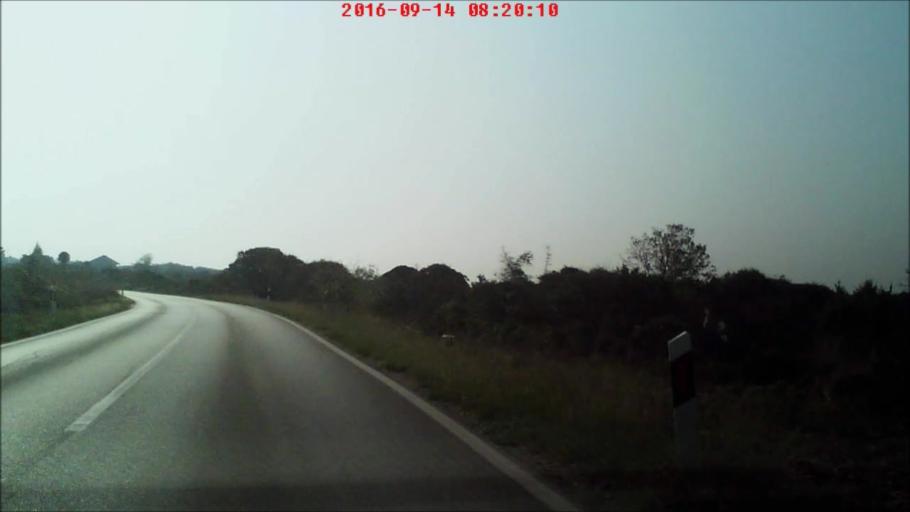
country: HR
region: Zadarska
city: Nin
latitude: 44.2279
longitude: 15.1976
